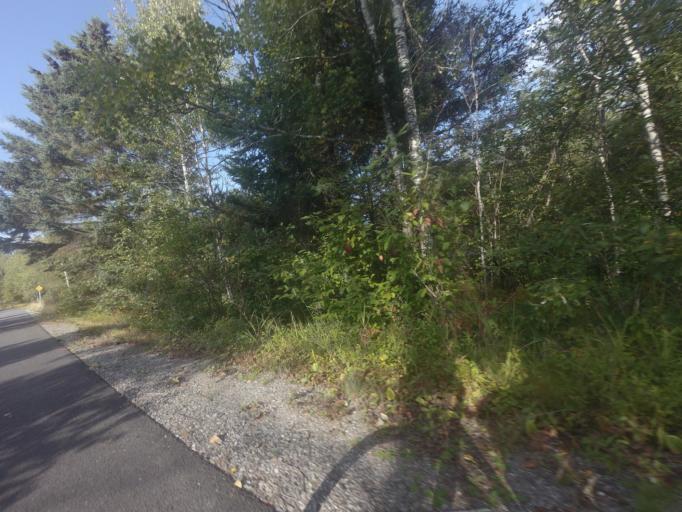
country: CA
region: Quebec
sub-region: Laurentides
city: Labelle
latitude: 46.3140
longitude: -74.7677
